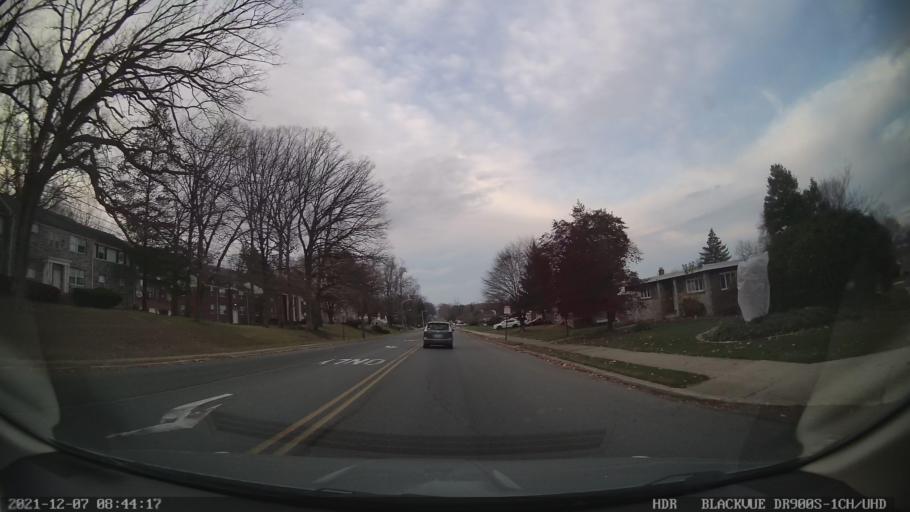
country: US
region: Pennsylvania
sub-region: Berks County
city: Hyde Park
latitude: 40.3651
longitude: -75.9024
